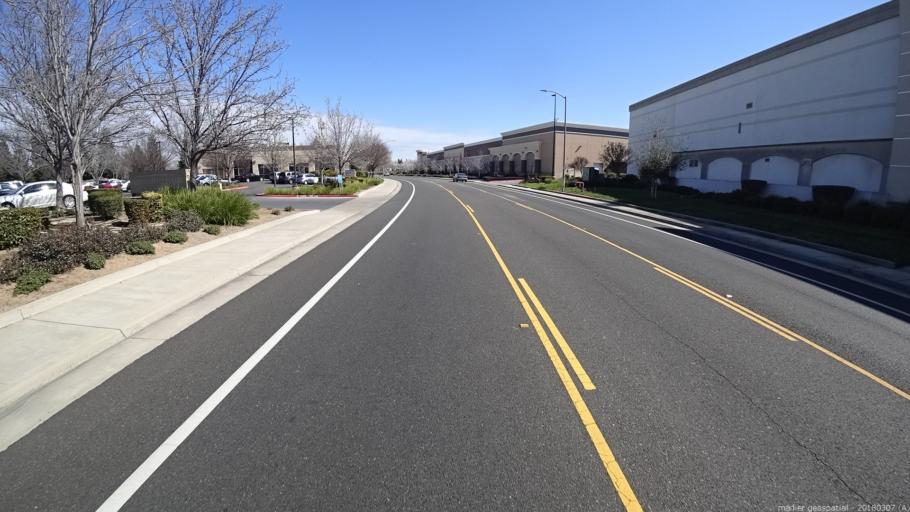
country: US
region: California
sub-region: Sacramento County
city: Florin
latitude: 38.4589
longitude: -121.4089
